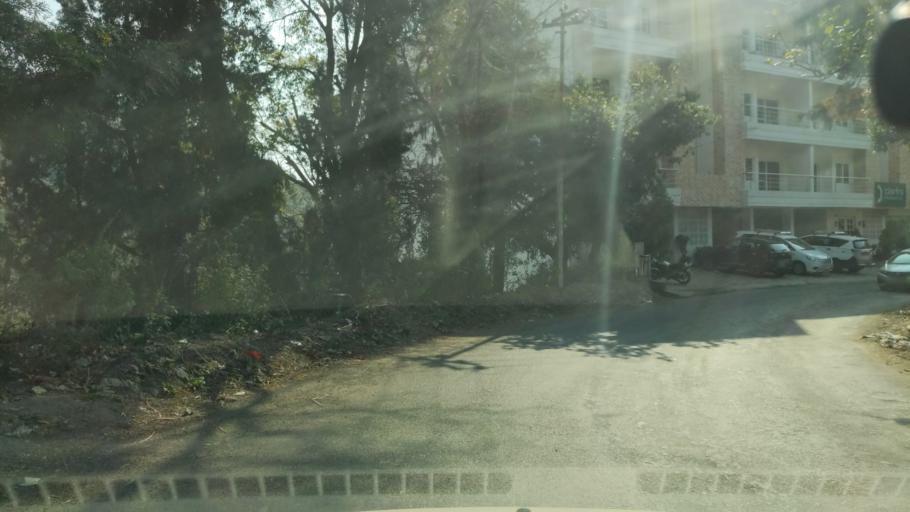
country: IN
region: Uttarakhand
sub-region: Naini Tal
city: Bhowali
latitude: 29.3896
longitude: 79.5317
